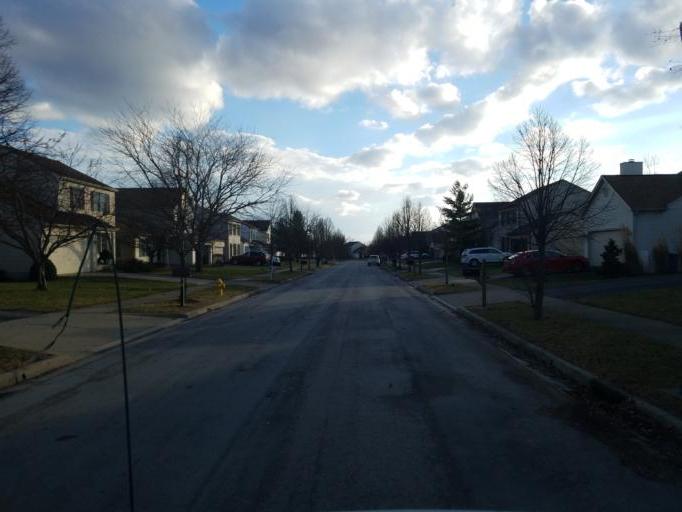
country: US
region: Ohio
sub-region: Delaware County
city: Delaware
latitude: 40.3153
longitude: -83.1071
